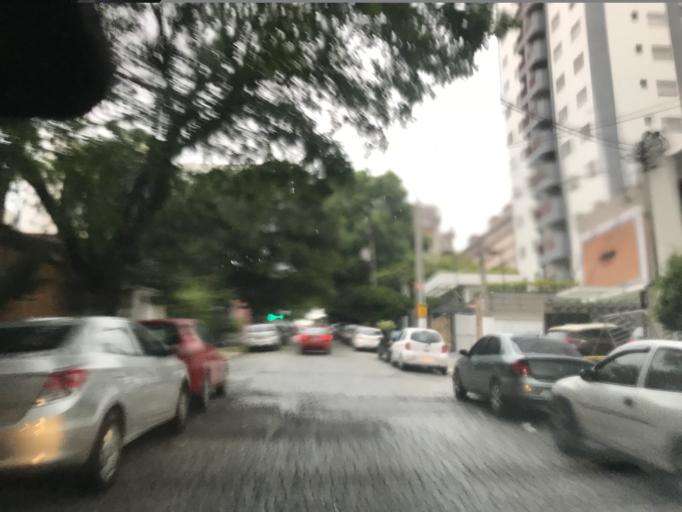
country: BR
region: Sao Paulo
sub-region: Sao Paulo
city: Sao Paulo
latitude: -23.5323
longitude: -46.6879
